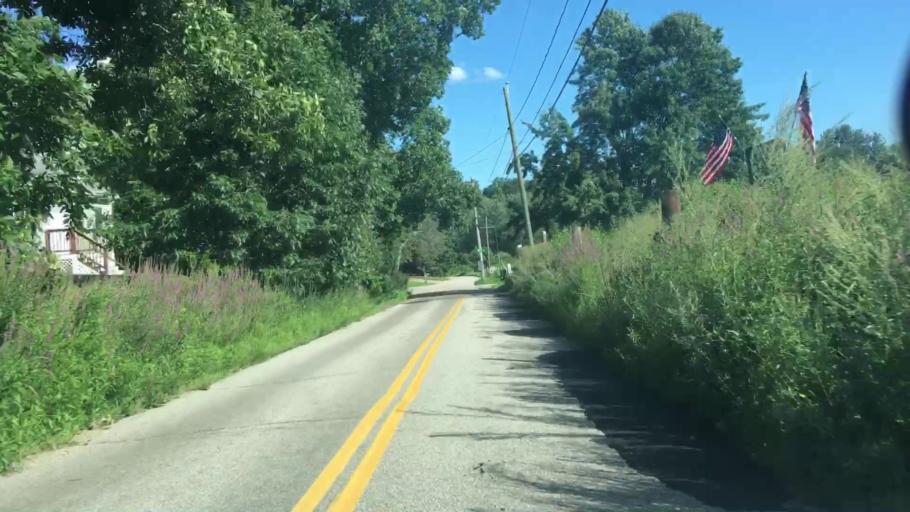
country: US
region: New Hampshire
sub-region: Strafford County
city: Dover
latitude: 43.1569
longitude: -70.8683
